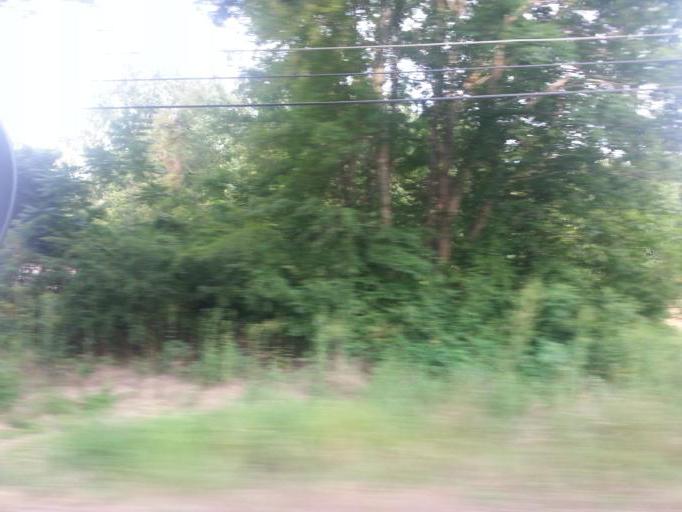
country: US
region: Tennessee
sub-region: Morgan County
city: Coalfield
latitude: 36.0919
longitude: -84.4512
